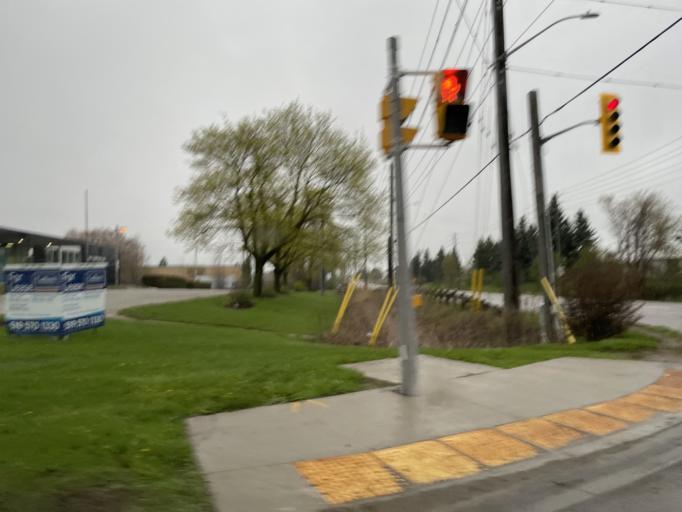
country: CA
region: Ontario
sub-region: Wellington County
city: Guelph
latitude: 43.5499
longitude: -80.2802
